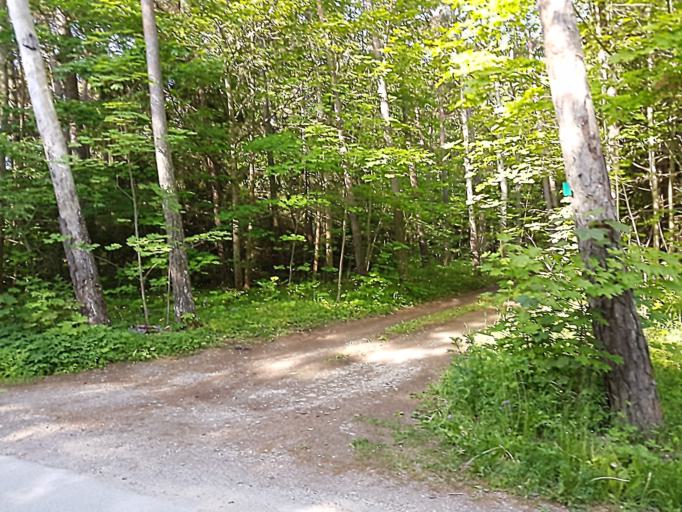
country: SE
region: Gotland
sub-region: Gotland
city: Visby
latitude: 57.6875
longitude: 18.3538
